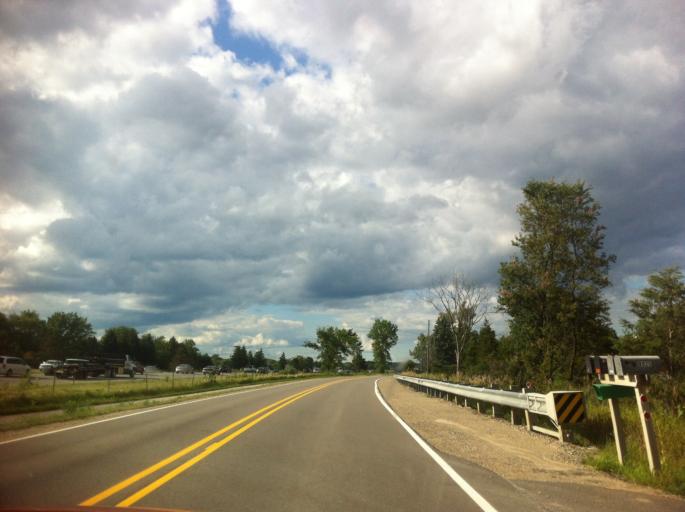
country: US
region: Michigan
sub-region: Livingston County
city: Whitmore Lake
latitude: 42.4846
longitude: -83.7564
